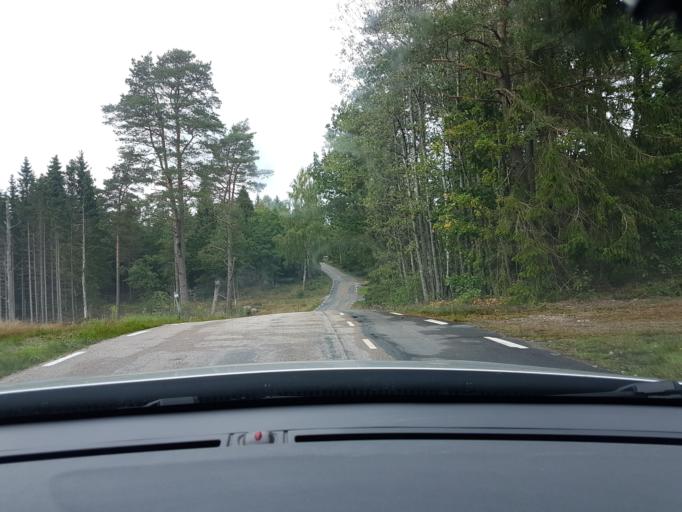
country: SE
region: Vaestra Goetaland
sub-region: Ale Kommun
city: Alvangen
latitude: 57.9027
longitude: 12.1787
